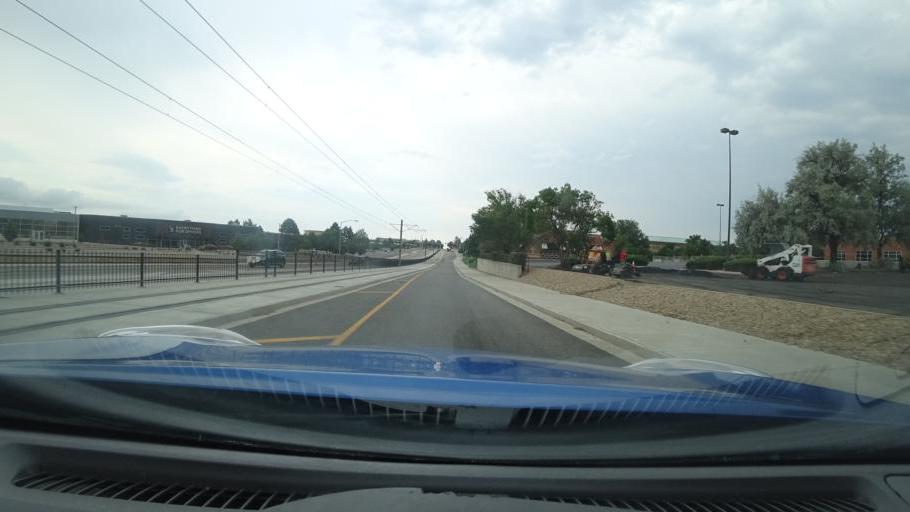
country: US
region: Colorado
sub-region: Adams County
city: Aurora
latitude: 39.7039
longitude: -104.8231
